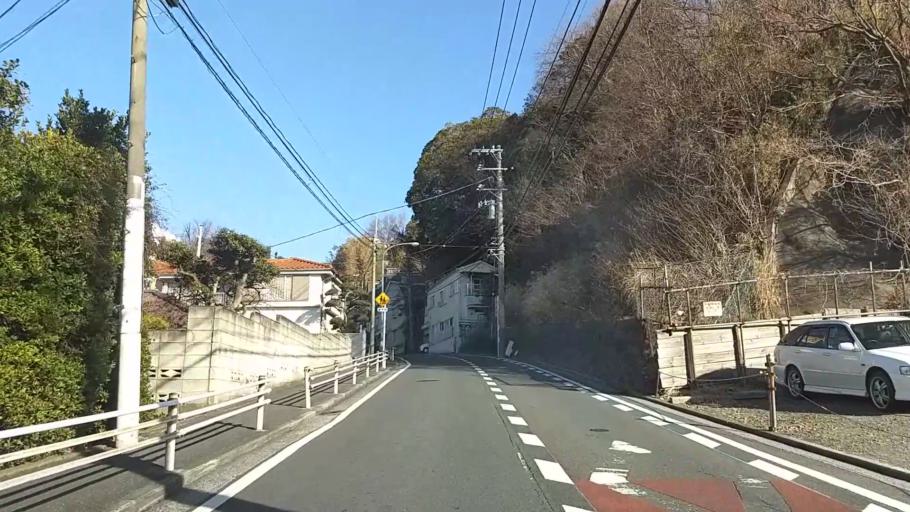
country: JP
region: Kanagawa
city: Yokohama
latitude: 35.4195
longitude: 139.6130
